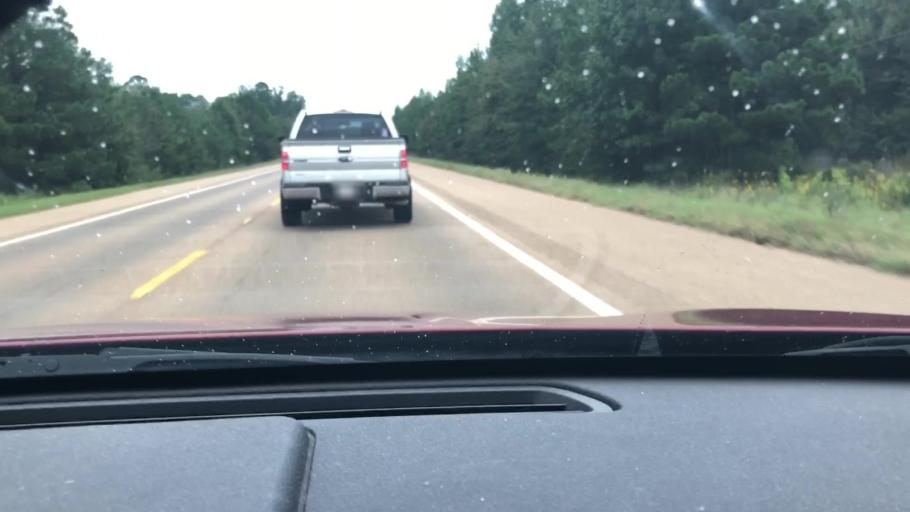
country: US
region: Arkansas
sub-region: Lafayette County
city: Stamps
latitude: 33.3666
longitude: -93.5266
